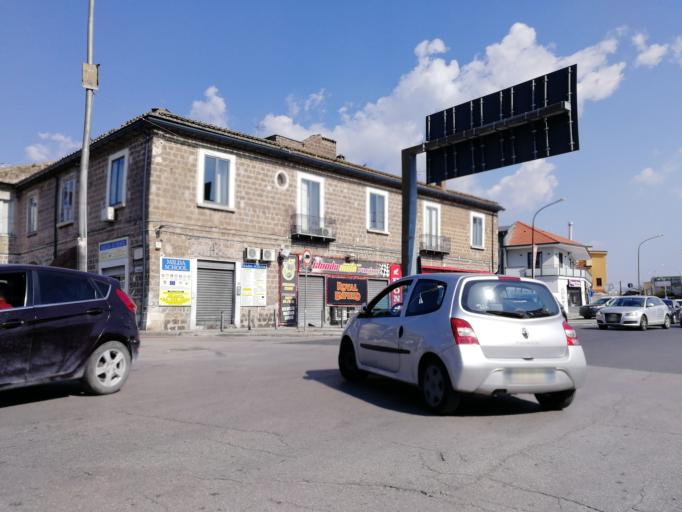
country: IT
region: Campania
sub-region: Provincia di Caserta
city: San Prisco
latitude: 41.0816
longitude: 14.2695
